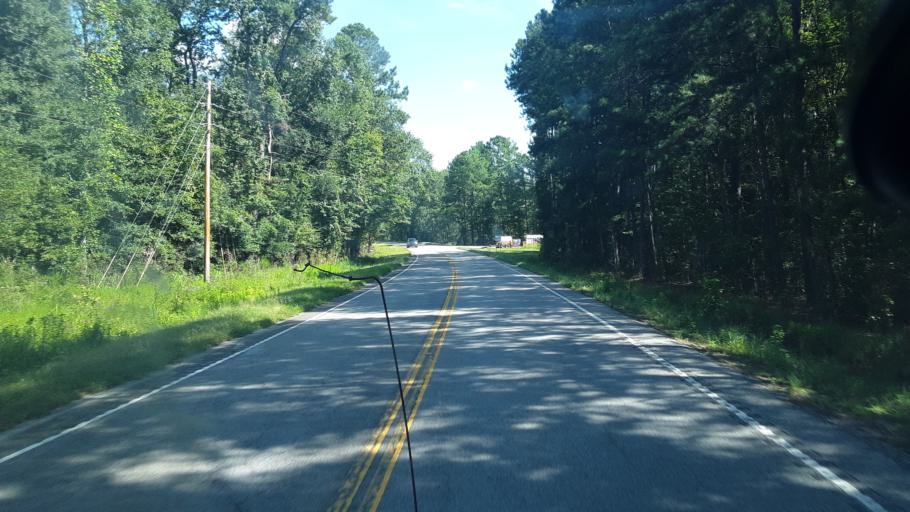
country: US
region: South Carolina
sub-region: Hampton County
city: Varnville
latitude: 32.8006
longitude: -81.0528
